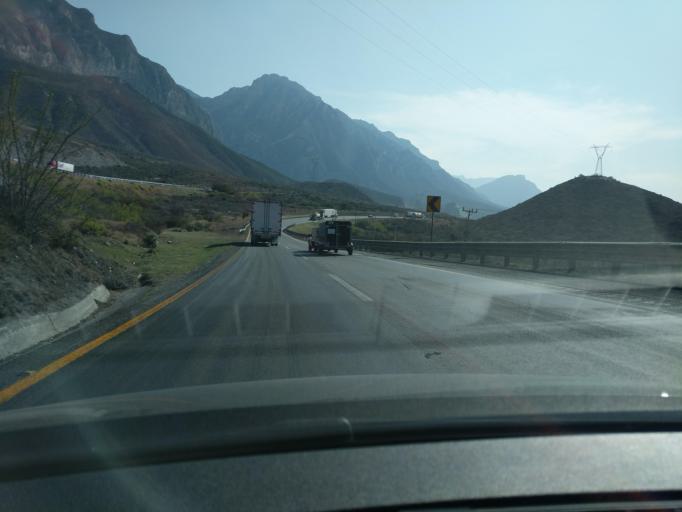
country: MX
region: Nuevo Leon
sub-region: Garcia
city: Las Torres de Guadalupe
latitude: 25.6852
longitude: -100.6598
